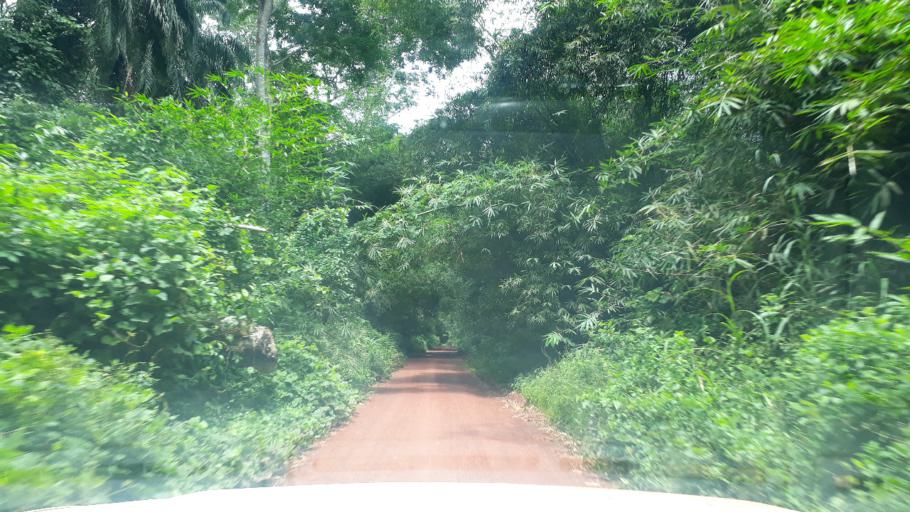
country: CD
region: Eastern Province
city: Aketi
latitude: 2.9175
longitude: 24.0641
